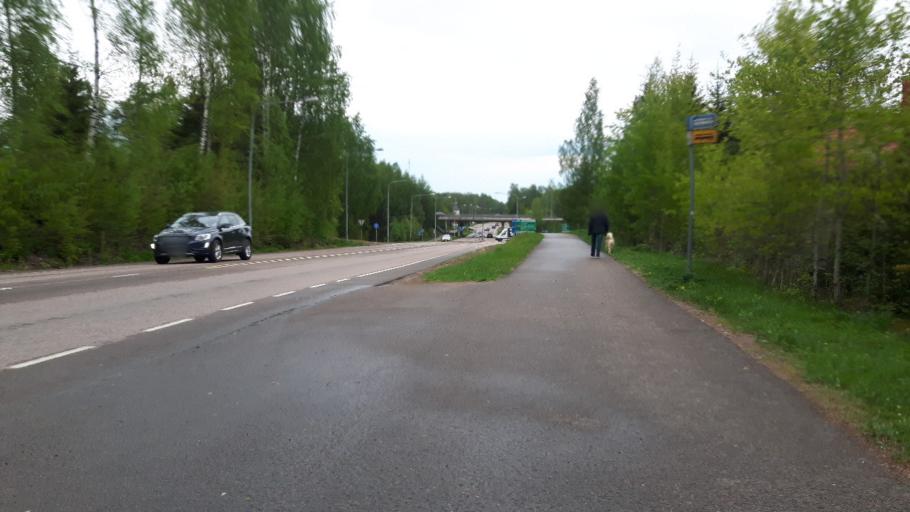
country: FI
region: Kymenlaakso
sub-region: Kotka-Hamina
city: Hamina
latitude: 60.5637
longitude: 27.1557
